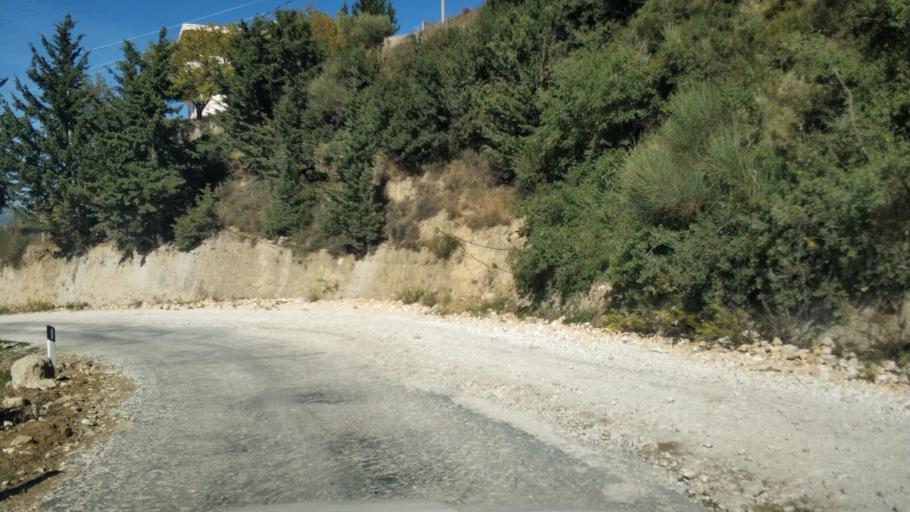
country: AL
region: Vlore
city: Vlore
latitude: 40.4472
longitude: 19.5183
